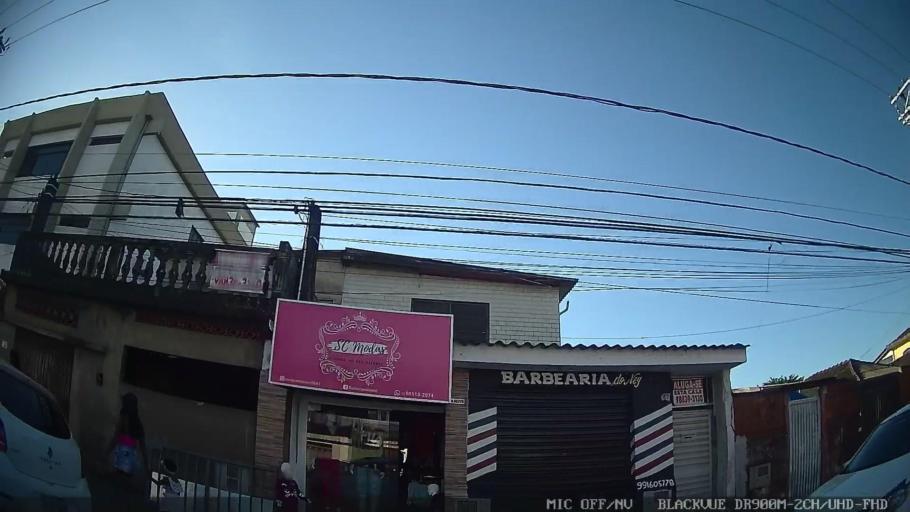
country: BR
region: Sao Paulo
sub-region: Santos
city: Santos
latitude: -23.9578
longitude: -46.2928
